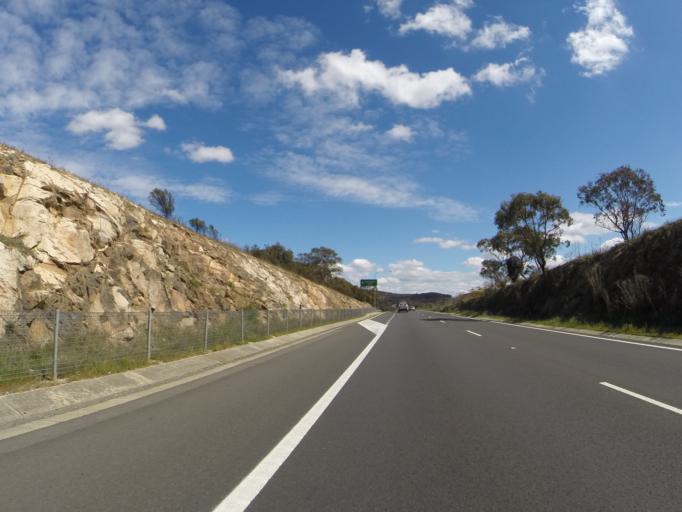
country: AU
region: New South Wales
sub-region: Goulburn Mulwaree
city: Goulburn
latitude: -34.7381
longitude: 149.7825
